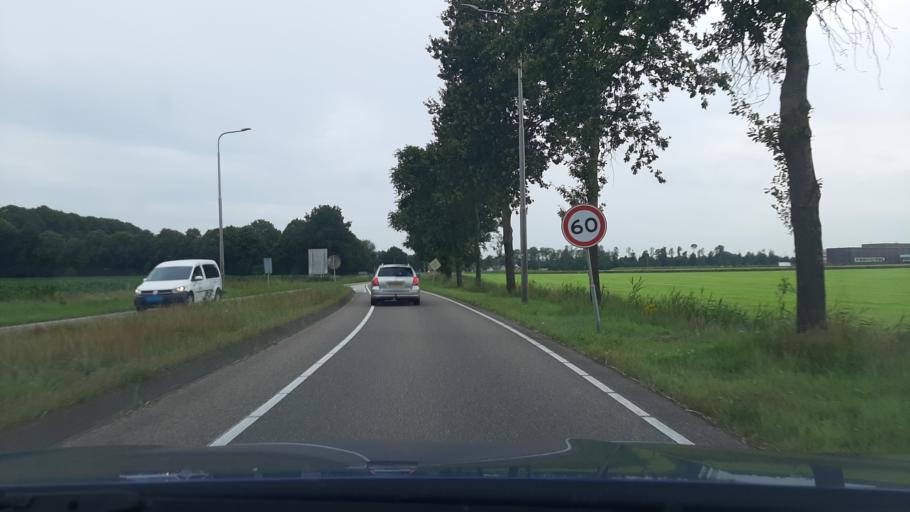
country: NL
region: Groningen
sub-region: Gemeente  Oldambt
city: Winschoten
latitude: 53.1831
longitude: 6.9707
